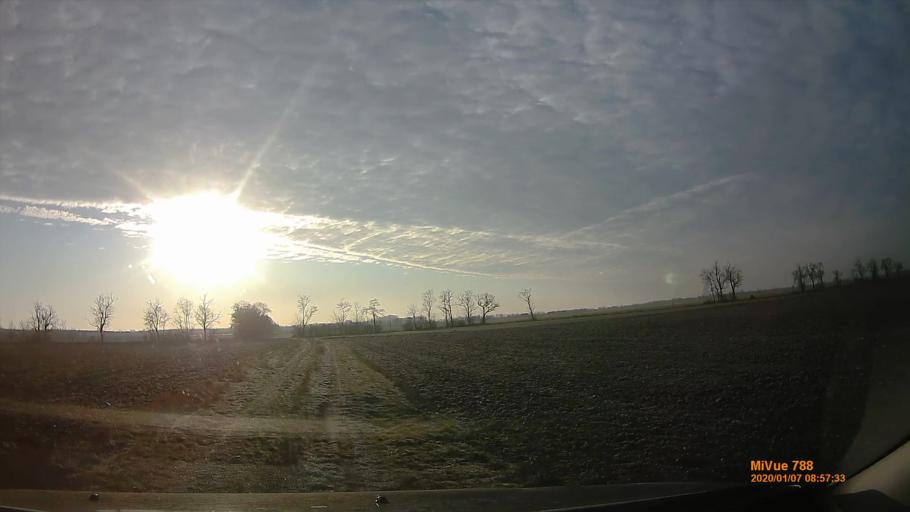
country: HU
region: Gyor-Moson-Sopron
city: Rajka
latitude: 47.9871
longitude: 17.1805
